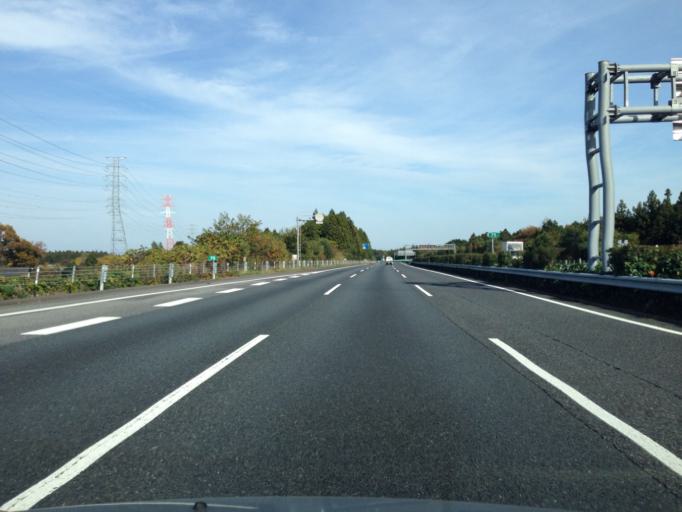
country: JP
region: Ibaraki
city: Tomobe
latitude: 36.3273
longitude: 140.3514
